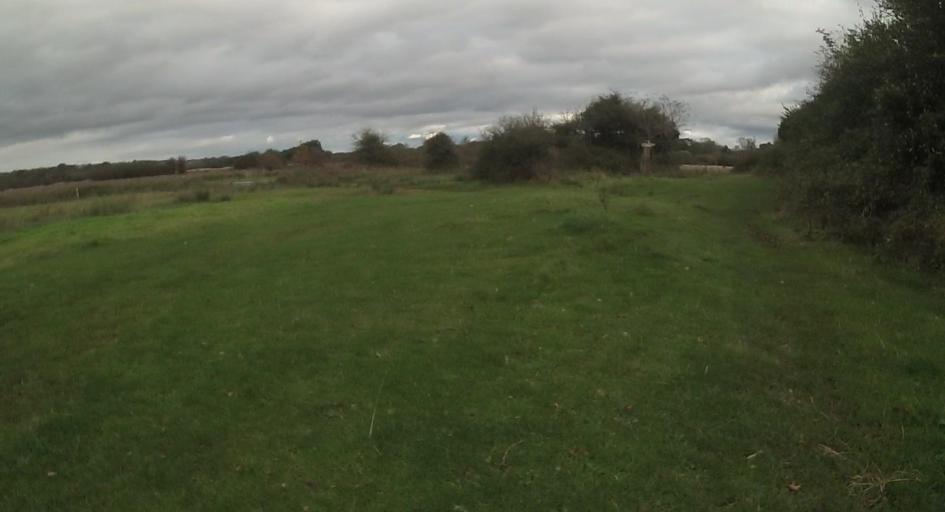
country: GB
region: England
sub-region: Hampshire
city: Andover
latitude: 51.1677
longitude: -1.4104
